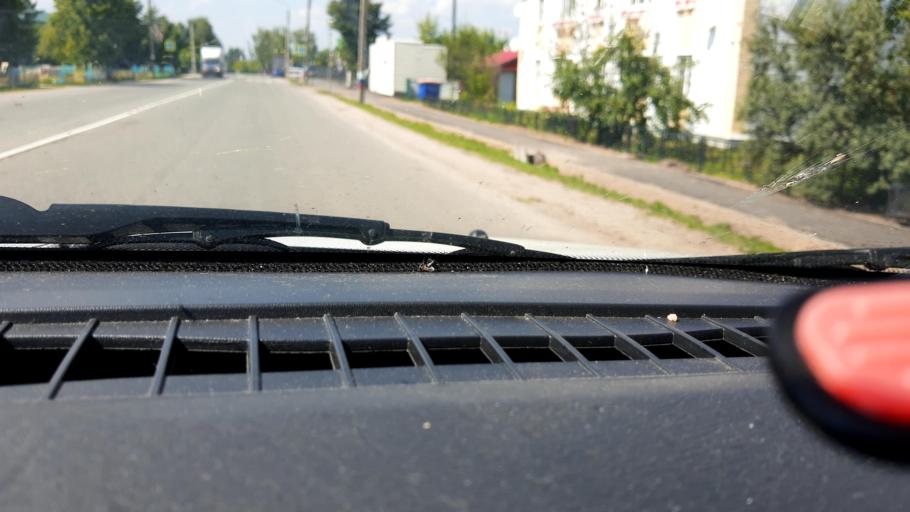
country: RU
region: Nizjnij Novgorod
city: Sharanga
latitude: 57.1789
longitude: 46.5404
